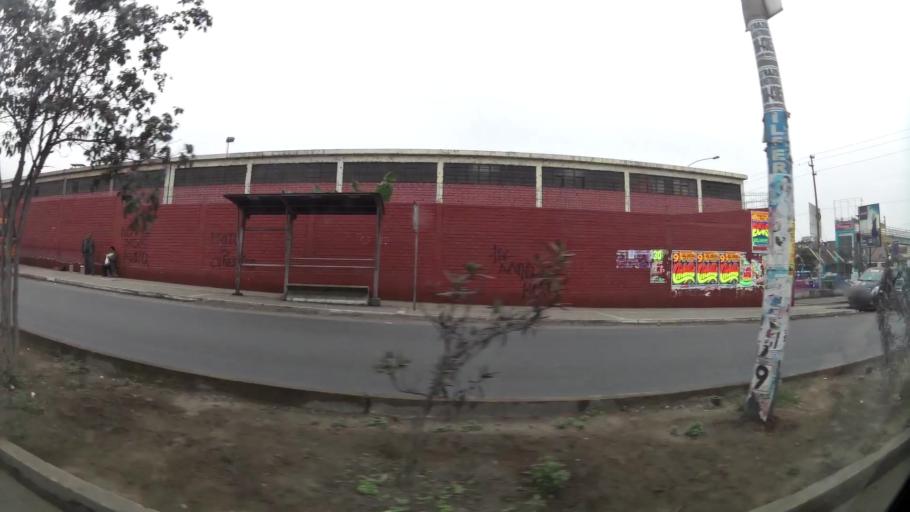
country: PE
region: Lima
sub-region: Lima
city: Urb. Santo Domingo
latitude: -11.9164
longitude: -77.0405
